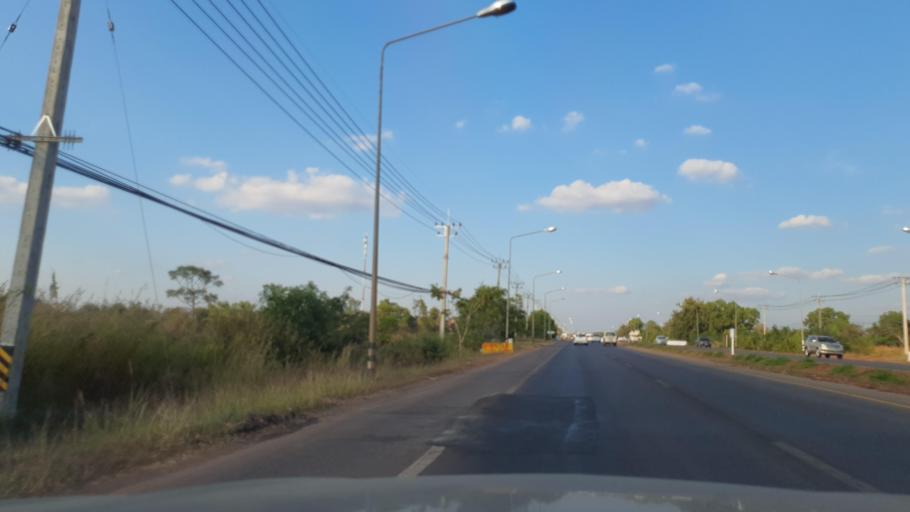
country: TH
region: Sakon Nakhon
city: Sakon Nakhon
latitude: 17.2341
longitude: 104.1085
